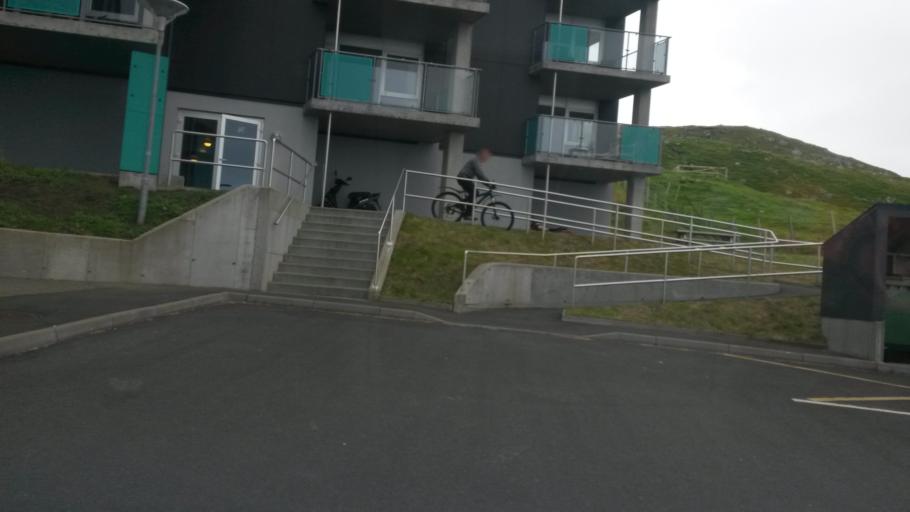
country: FO
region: Streymoy
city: Argir
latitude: 62.0025
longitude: -6.8063
